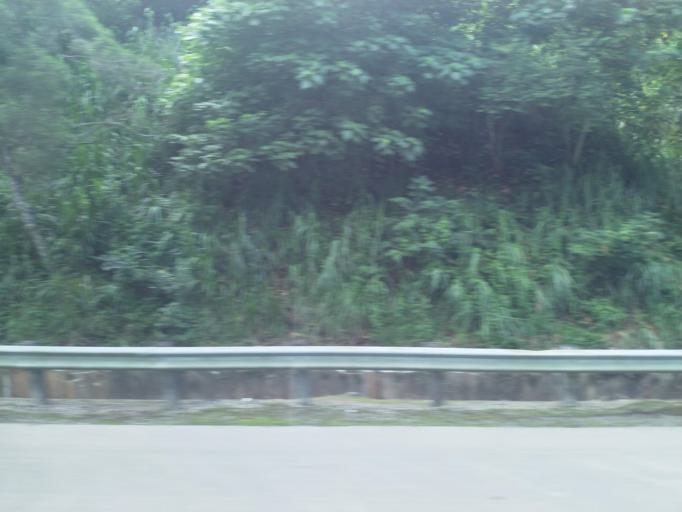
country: TW
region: Taiwan
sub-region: Pingtung
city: Pingtung
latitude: 22.7932
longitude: 120.4330
